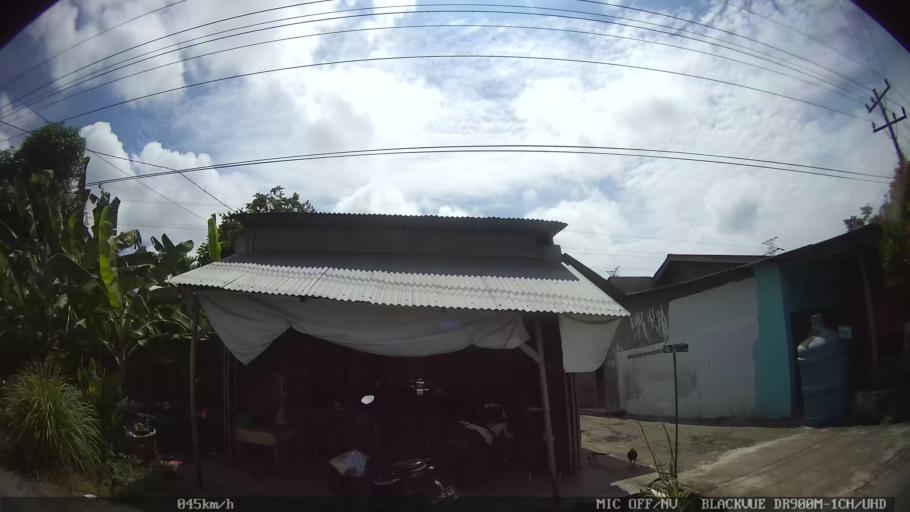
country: ID
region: North Sumatra
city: Percut
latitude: 3.6052
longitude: 98.7878
